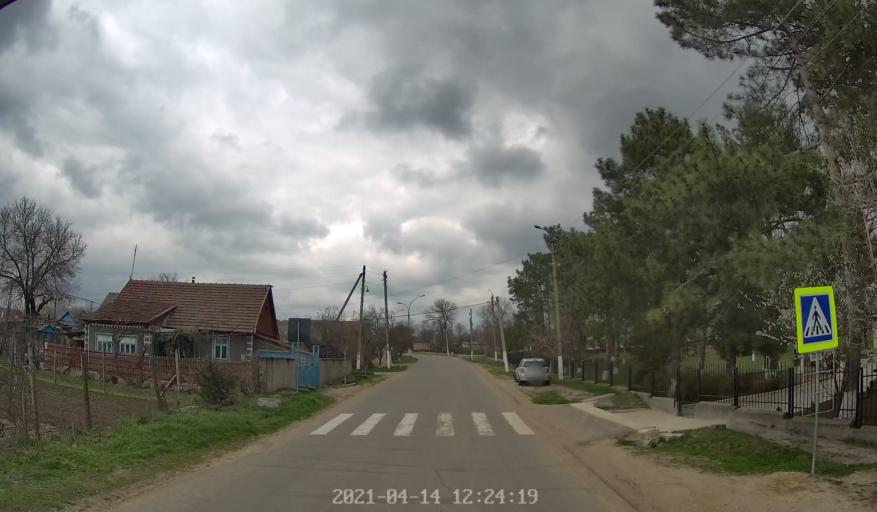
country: MD
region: Criuleni
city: Criuleni
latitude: 47.1697
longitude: 29.1957
